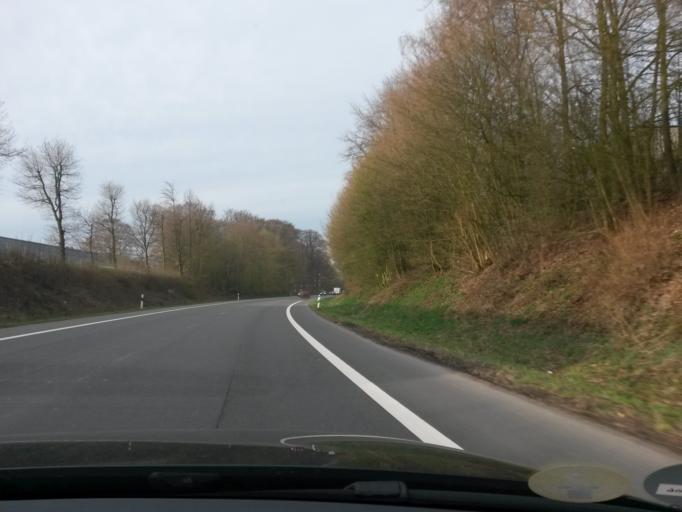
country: DE
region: North Rhine-Westphalia
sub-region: Regierungsbezirk Arnsberg
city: Luedenscheid
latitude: 51.2528
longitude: 7.6015
